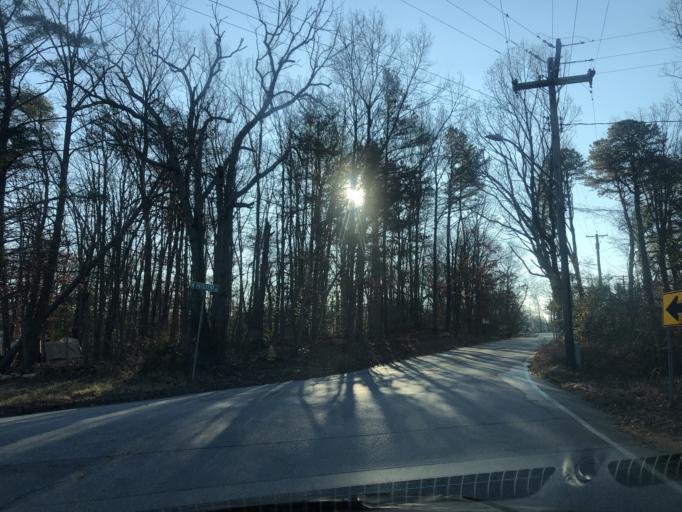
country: US
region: Maryland
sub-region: Anne Arundel County
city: Odenton
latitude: 39.0768
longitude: -76.7097
